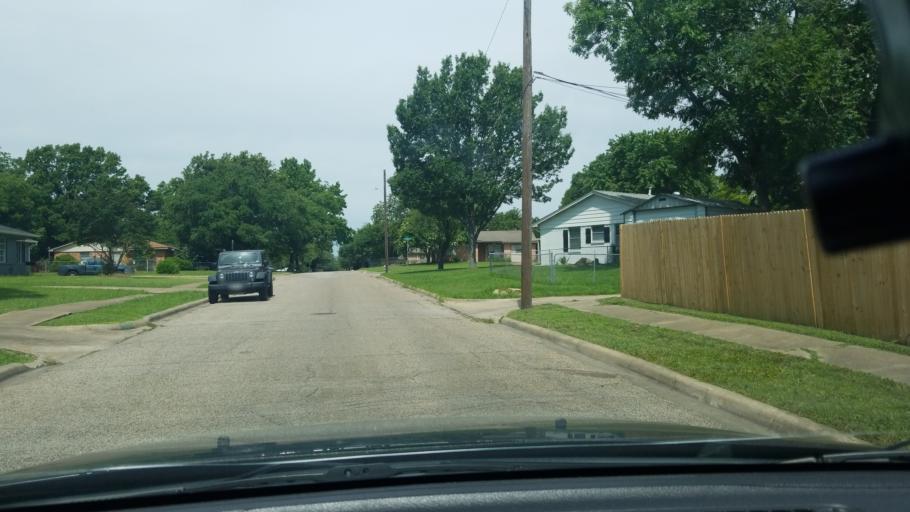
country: US
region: Texas
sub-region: Dallas County
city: Mesquite
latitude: 32.7535
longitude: -96.5791
